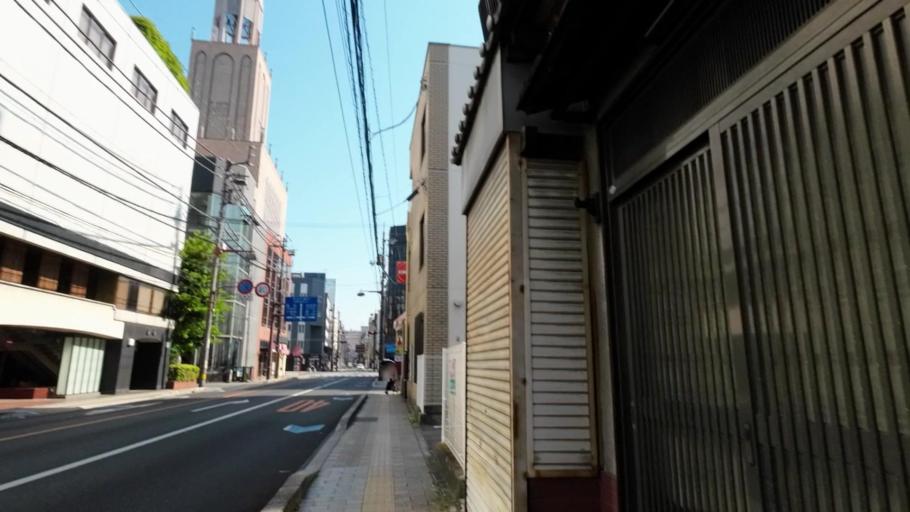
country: JP
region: Ehime
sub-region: Shikoku-chuo Shi
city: Matsuyama
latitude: 33.8422
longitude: 132.7723
